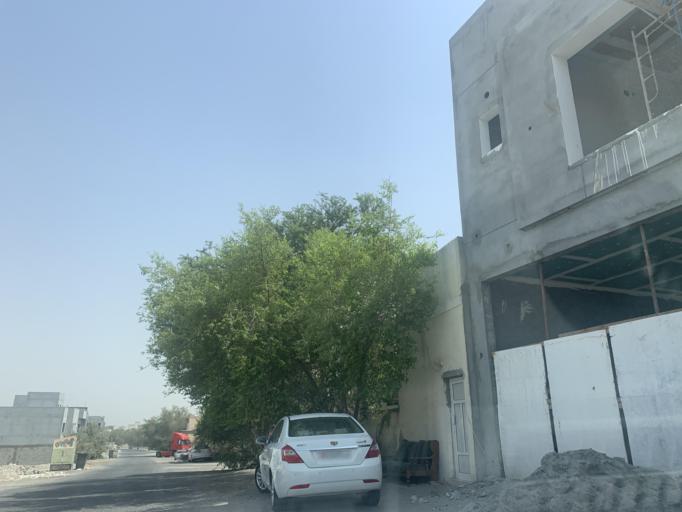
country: BH
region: Northern
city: Madinat `Isa
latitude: 26.1922
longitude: 50.4893
